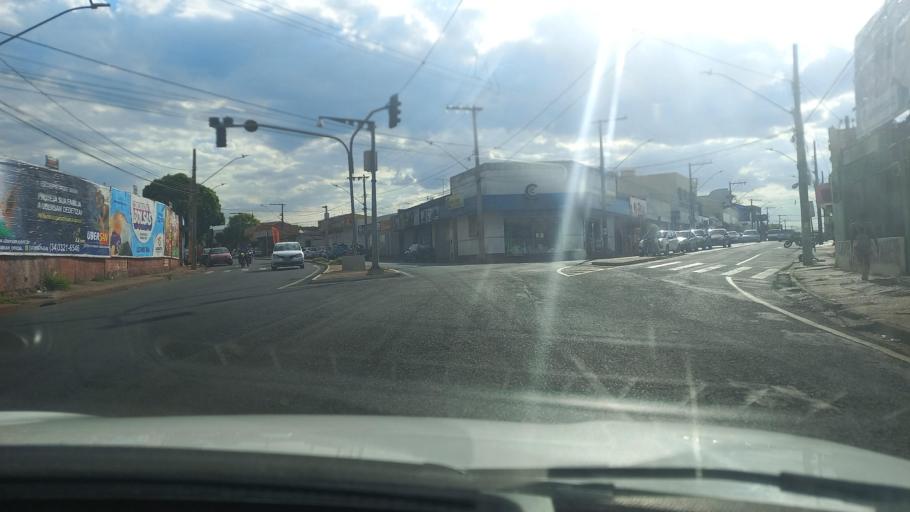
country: BR
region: Minas Gerais
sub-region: Uberaba
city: Uberaba
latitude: -19.7622
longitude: -47.9157
